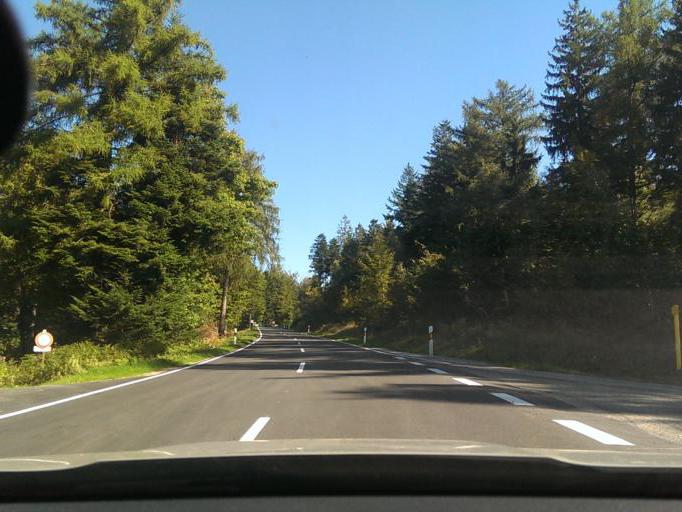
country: DE
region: Baden-Wuerttemberg
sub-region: Karlsruhe Region
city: Dobel
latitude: 48.8039
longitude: 8.4807
